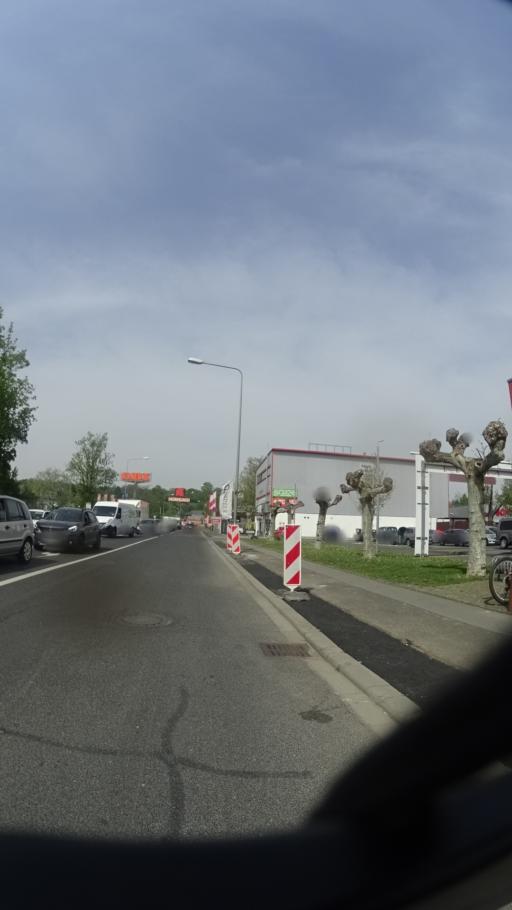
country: DE
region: Hesse
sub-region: Regierungsbezirk Darmstadt
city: Wiesbaden
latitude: 50.0491
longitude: 8.2201
